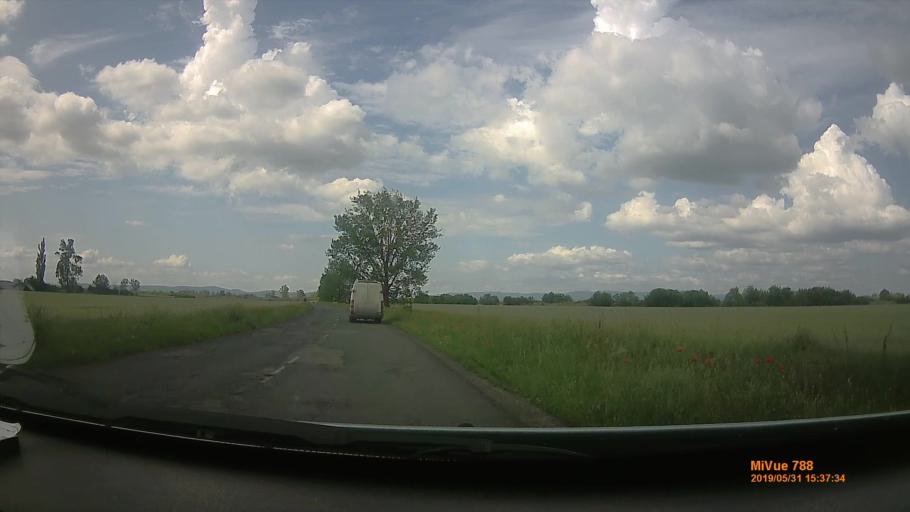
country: HU
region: Borsod-Abauj-Zemplen
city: Prugy
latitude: 48.0931
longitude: 21.2415
